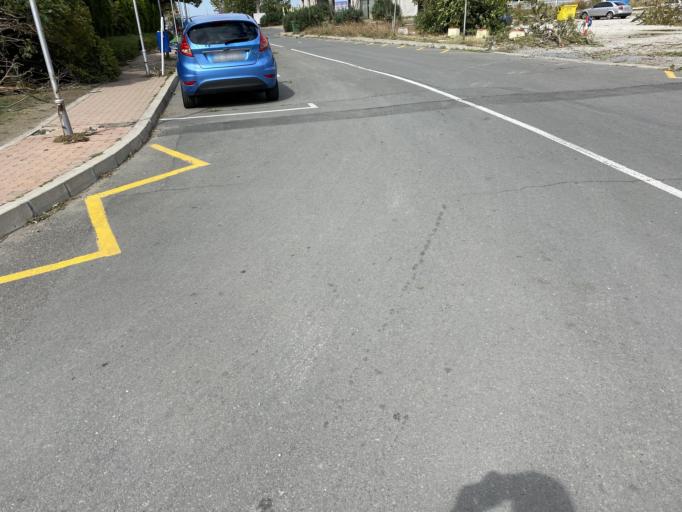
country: BG
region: Burgas
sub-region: Obshtina Pomorie
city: Pomorie
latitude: 42.5656
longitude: 27.6384
